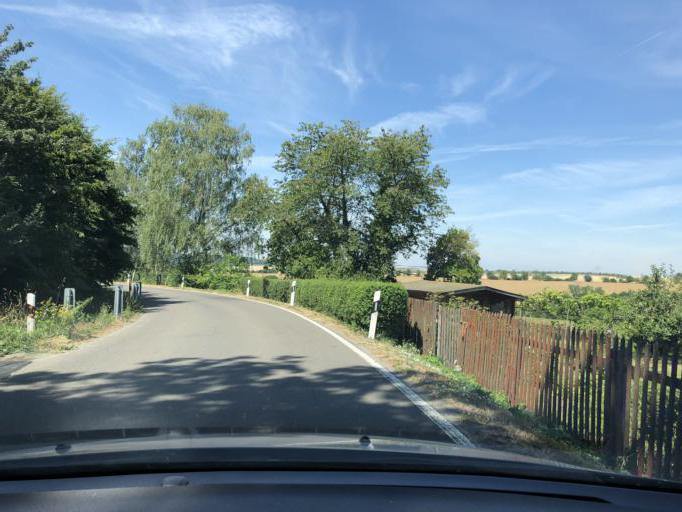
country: DE
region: Thuringia
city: Thierschneck
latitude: 51.0656
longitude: 11.7532
